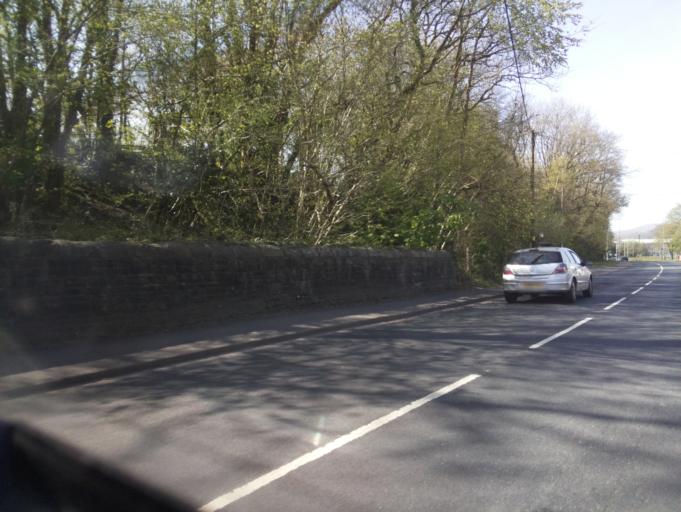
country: GB
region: Wales
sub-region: Caerphilly County Borough
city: Abertridwr
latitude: 51.5592
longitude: -3.2712
